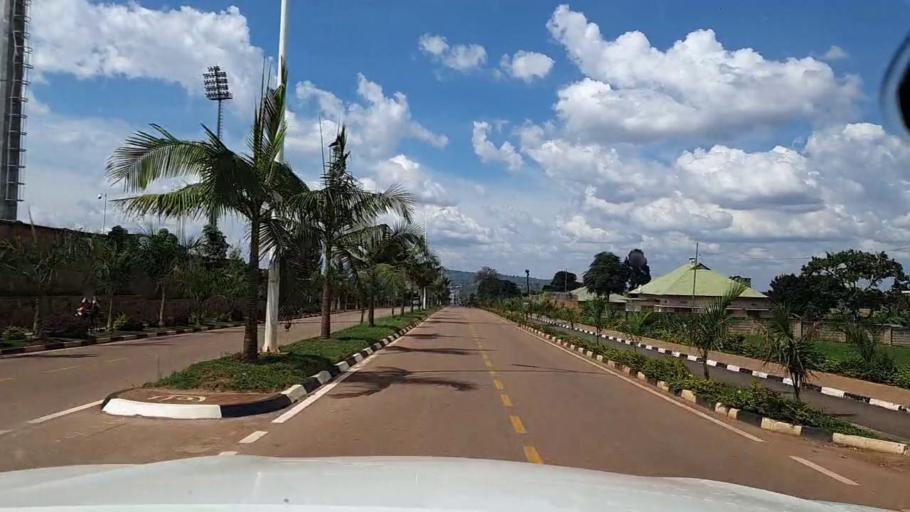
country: RW
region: Southern Province
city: Butare
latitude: -2.5974
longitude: 29.7426
